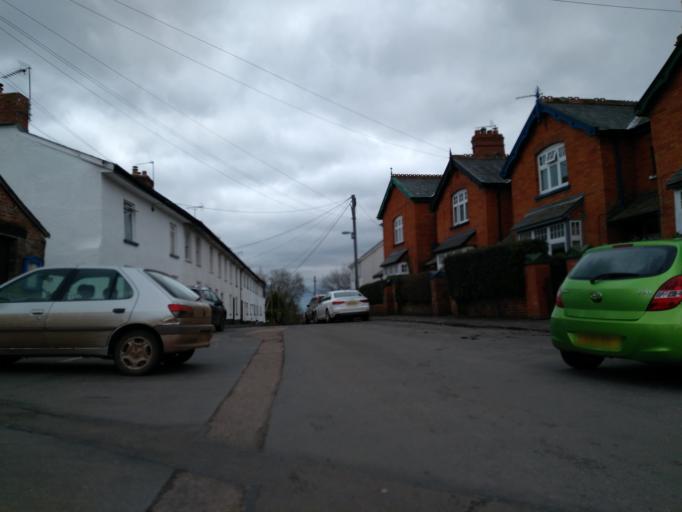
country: GB
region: England
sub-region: Devon
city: Bradninch
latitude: 50.8157
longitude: -3.4839
